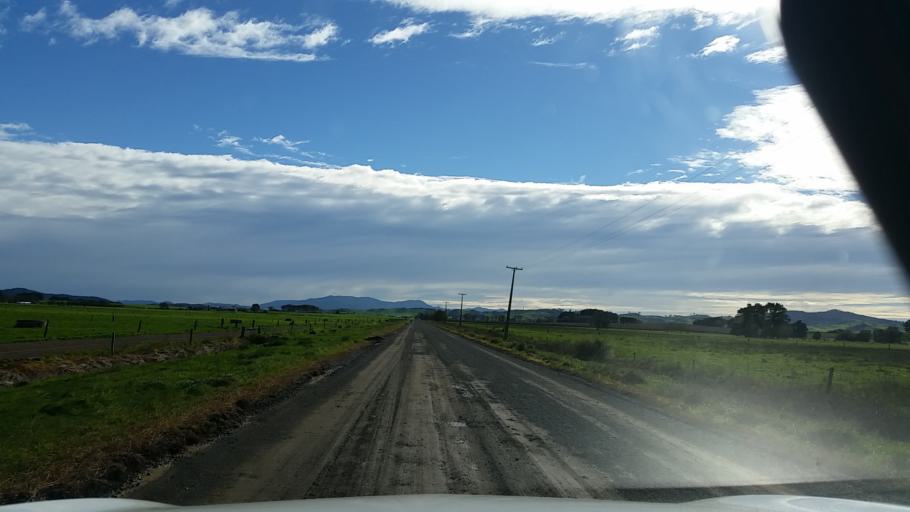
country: NZ
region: Waikato
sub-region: Hamilton City
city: Hamilton
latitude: -37.6406
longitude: 175.4313
